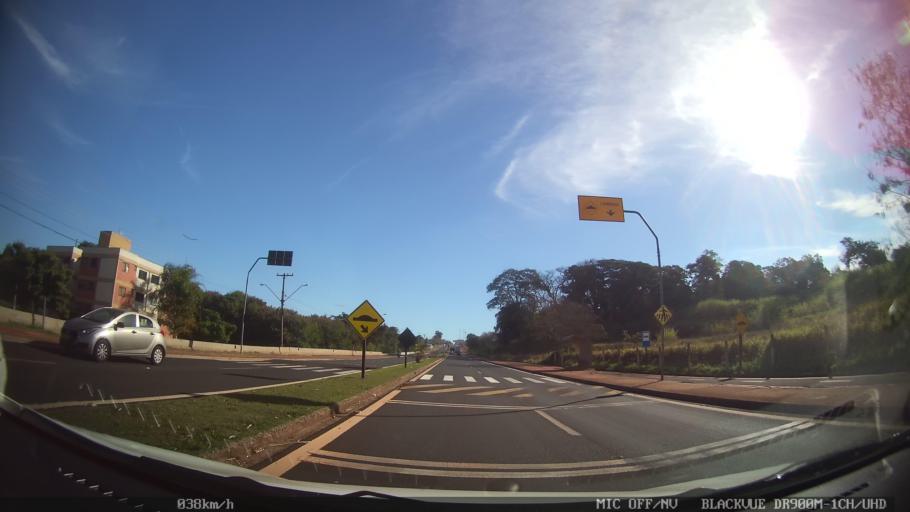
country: BR
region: Sao Paulo
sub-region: Araraquara
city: Araraquara
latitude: -21.7905
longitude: -48.1458
